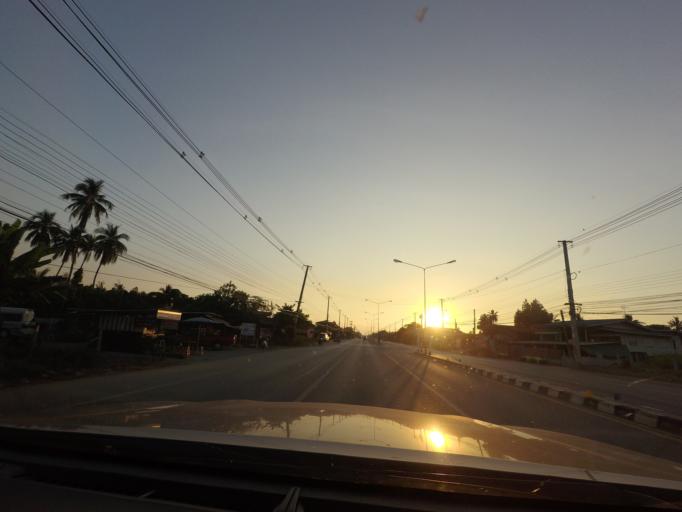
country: TH
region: Sukhothai
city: Sukhothai
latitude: 17.0599
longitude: 99.8375
